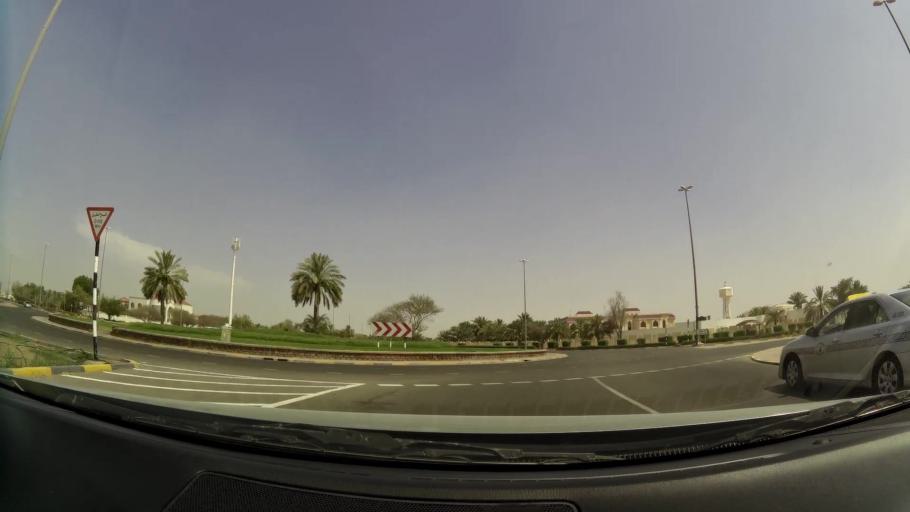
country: AE
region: Abu Dhabi
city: Al Ain
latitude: 24.2335
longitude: 55.7064
